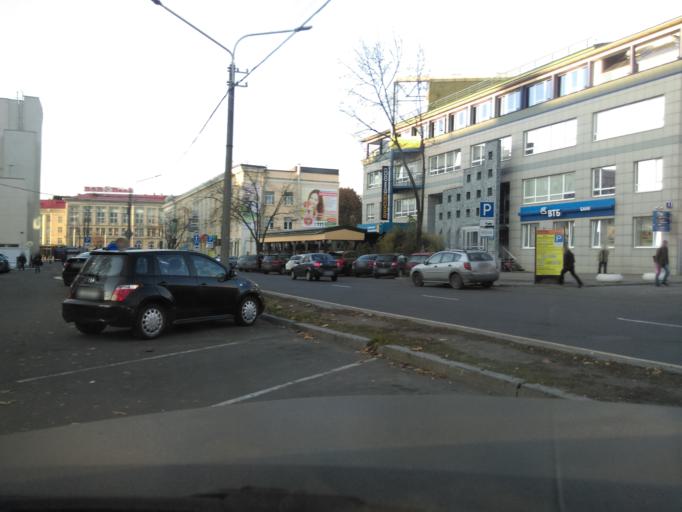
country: BY
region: Minsk
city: Minsk
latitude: 53.9155
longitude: 27.5880
